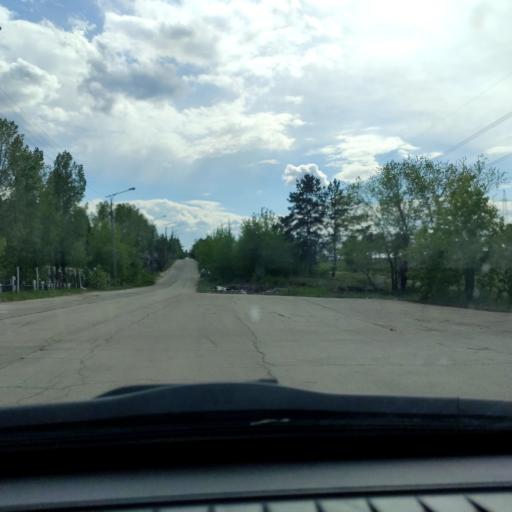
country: RU
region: Samara
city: Zhigulevsk
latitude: 53.5269
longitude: 49.5407
